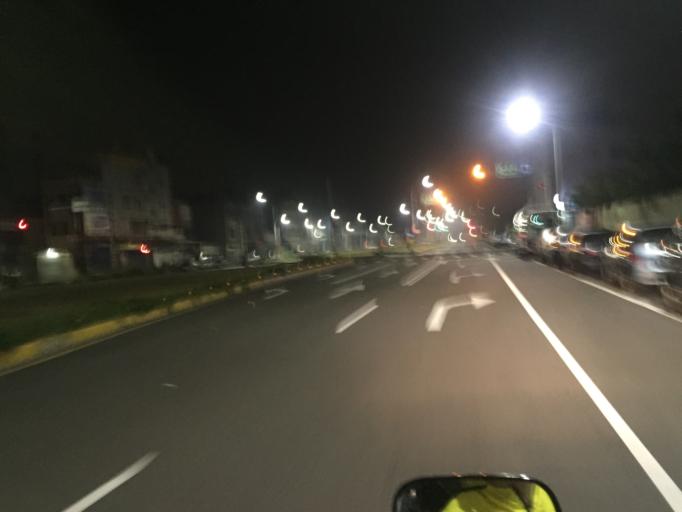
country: TW
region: Taiwan
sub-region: Hsinchu
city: Hsinchu
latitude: 24.8006
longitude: 120.9500
